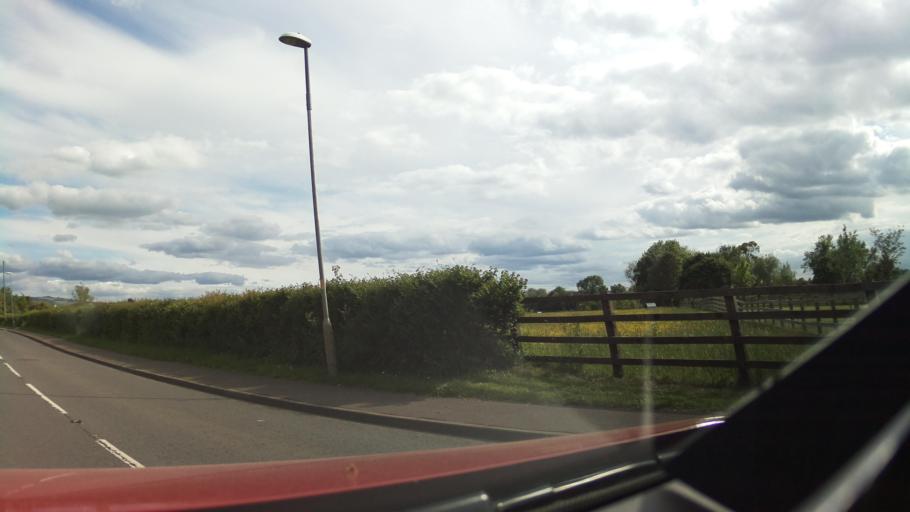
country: GB
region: England
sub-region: Worcestershire
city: South Littleton
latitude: 52.0896
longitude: -1.8602
